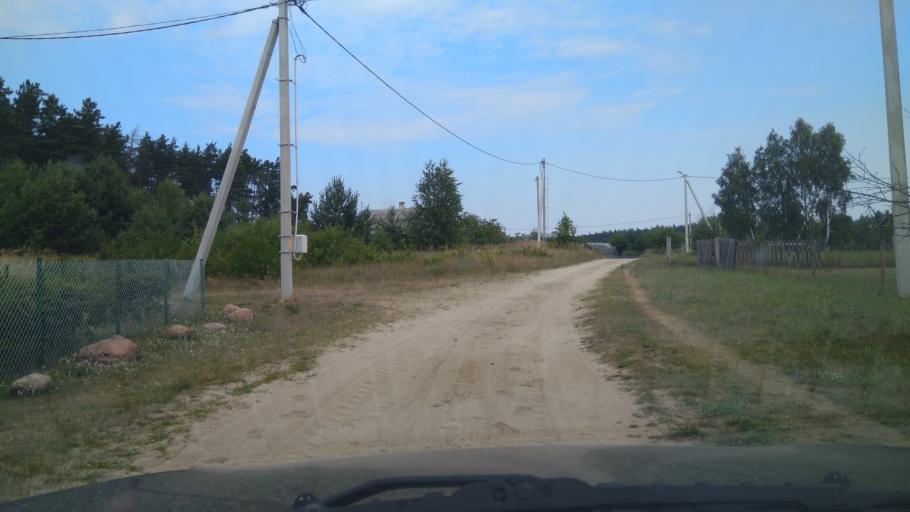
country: BY
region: Brest
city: Nyakhachava
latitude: 52.6078
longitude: 25.0923
